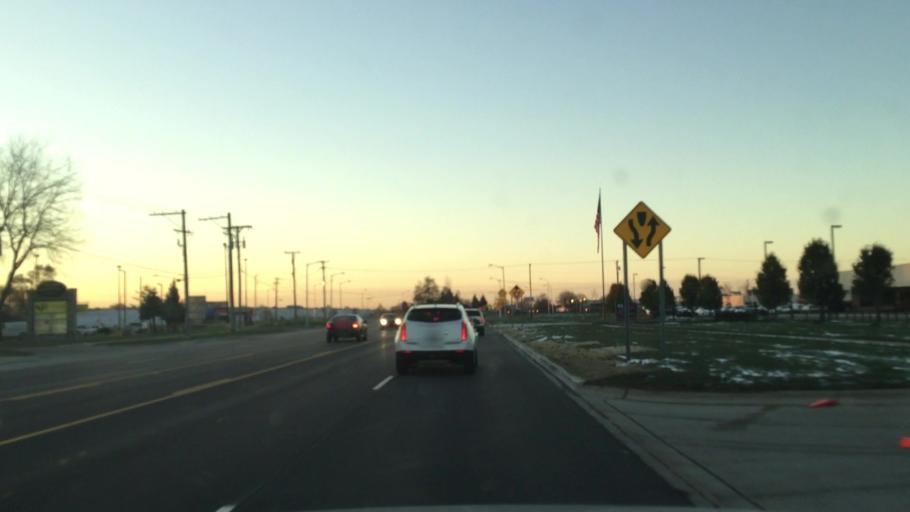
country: US
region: Michigan
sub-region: Macomb County
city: Utica
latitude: 42.6038
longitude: -83.0314
